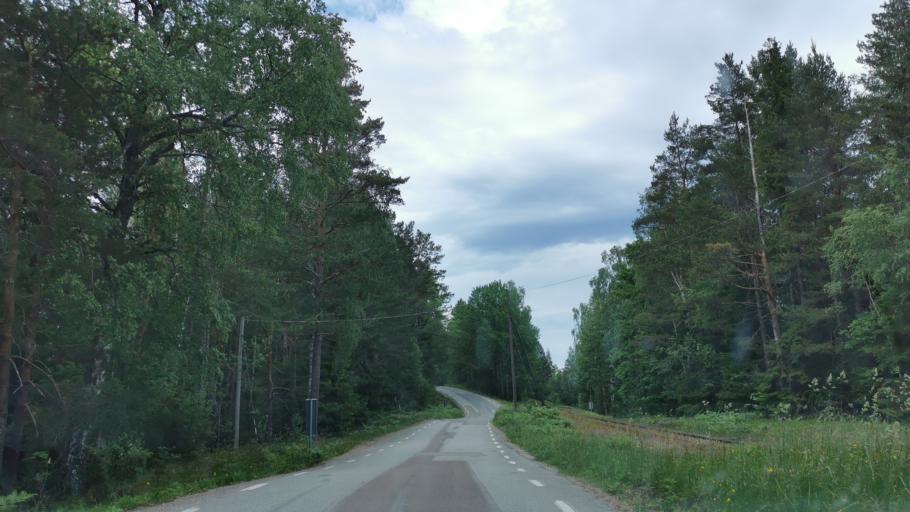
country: SE
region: Vaestra Goetaland
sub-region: Bengtsfors Kommun
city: Dals Langed
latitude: 58.8355
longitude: 12.4095
